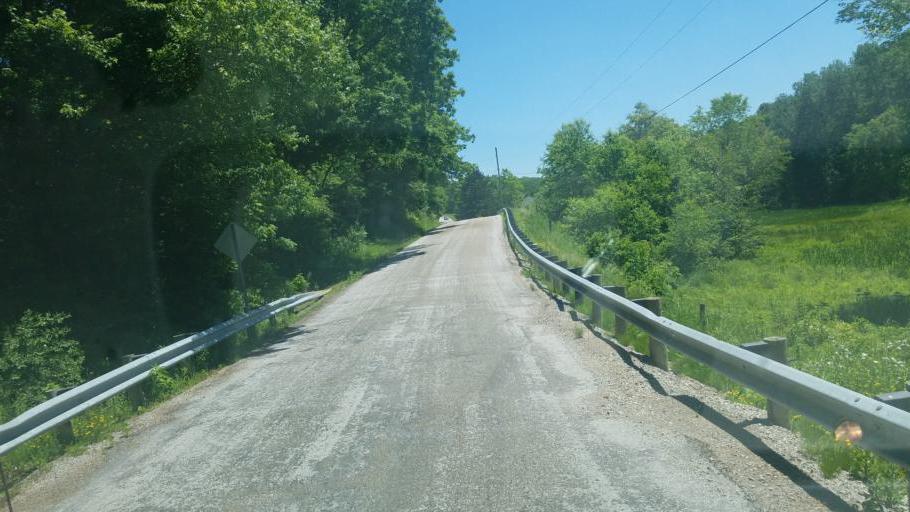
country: US
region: Ohio
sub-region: Coshocton County
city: Coshocton
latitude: 40.2704
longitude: -81.9653
